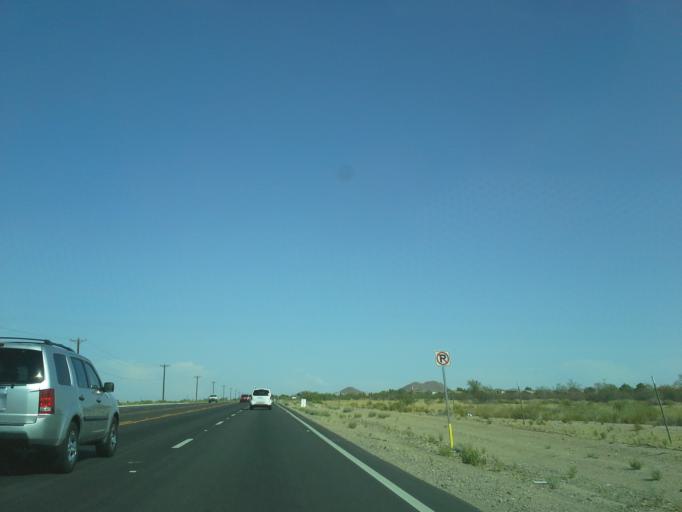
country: US
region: Arizona
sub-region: Maricopa County
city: Queen Creek
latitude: 33.1962
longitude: -111.6076
